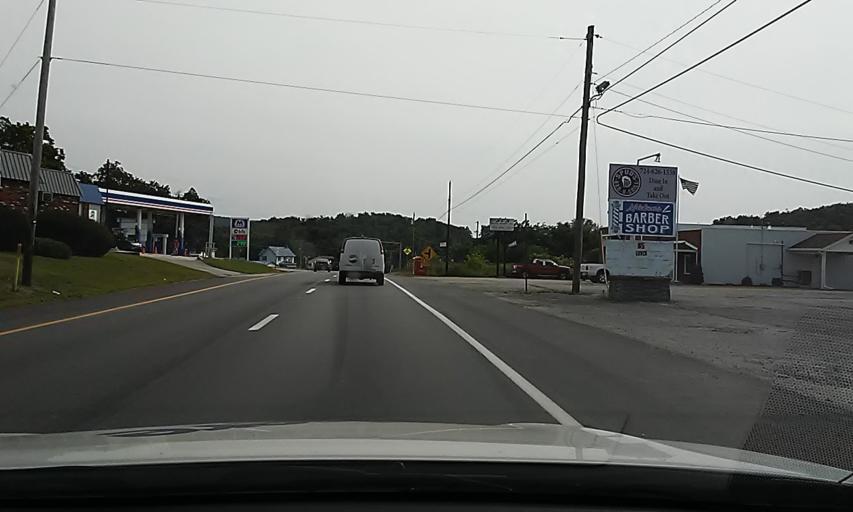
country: US
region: Pennsylvania
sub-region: Fayette County
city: Connellsville
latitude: 40.0059
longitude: -79.6027
